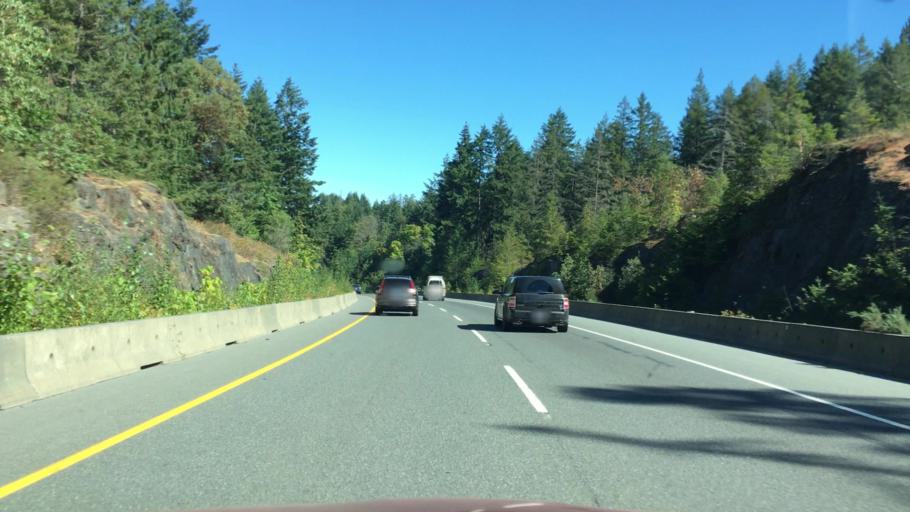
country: CA
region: British Columbia
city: Nanaimo
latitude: 49.1354
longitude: -123.9530
